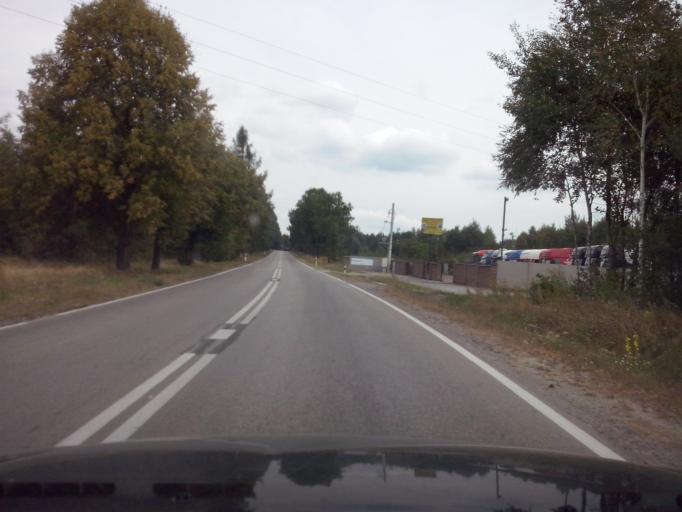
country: PL
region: Swietokrzyskie
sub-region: Powiat kielecki
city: Rakow
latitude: 50.6832
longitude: 21.0542
